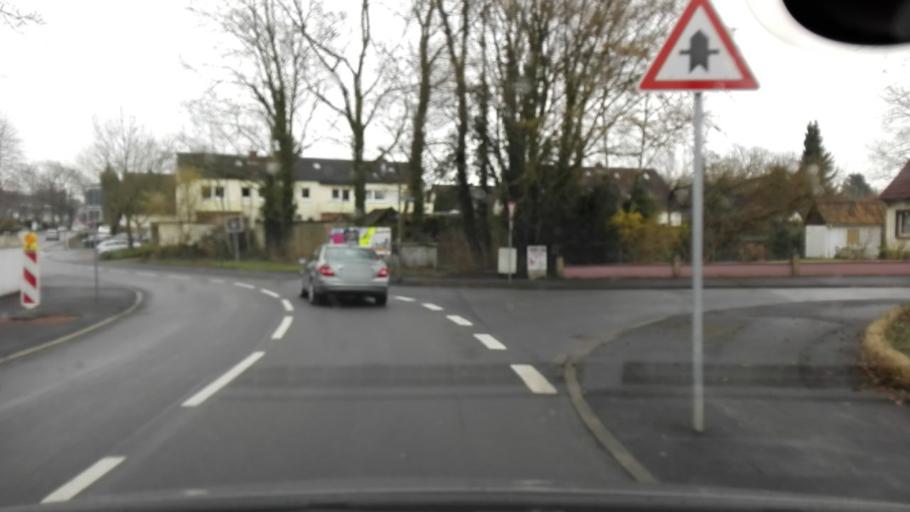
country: DE
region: North Rhine-Westphalia
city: Kamen
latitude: 51.5774
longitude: 7.6514
